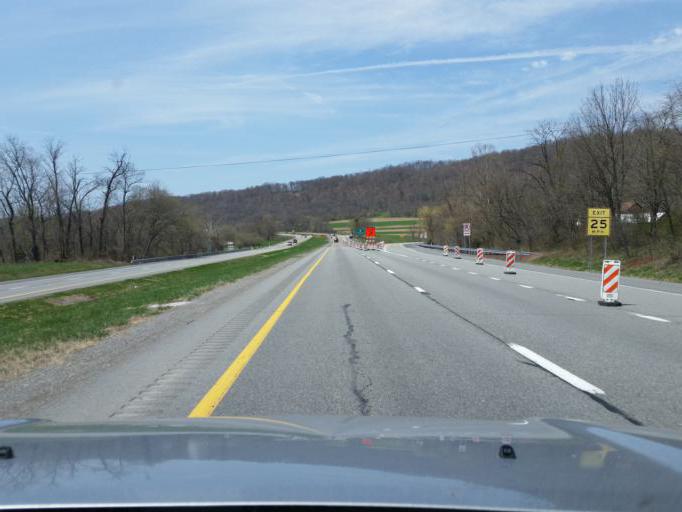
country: US
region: Pennsylvania
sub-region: Perry County
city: Newport
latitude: 40.5673
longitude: -77.1986
